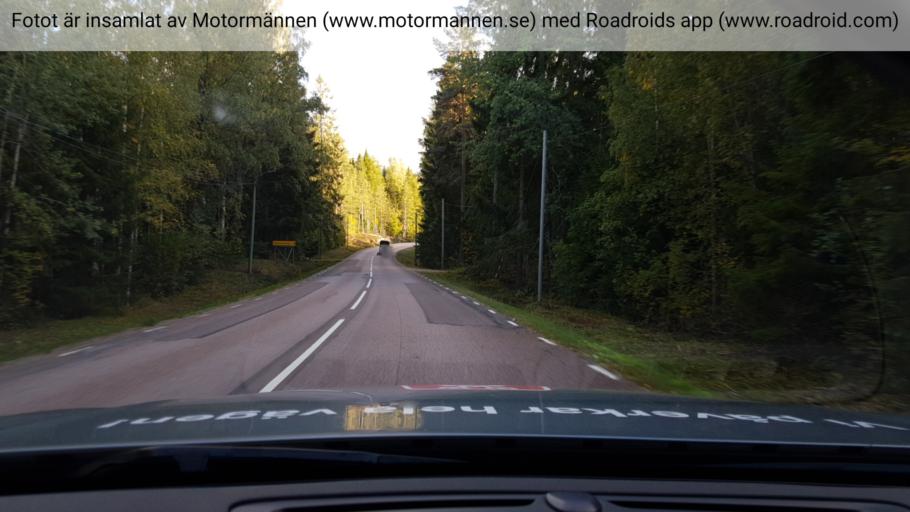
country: SE
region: Vaermland
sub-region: Karlstads Kommun
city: Molkom
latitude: 59.5112
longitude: 13.7954
